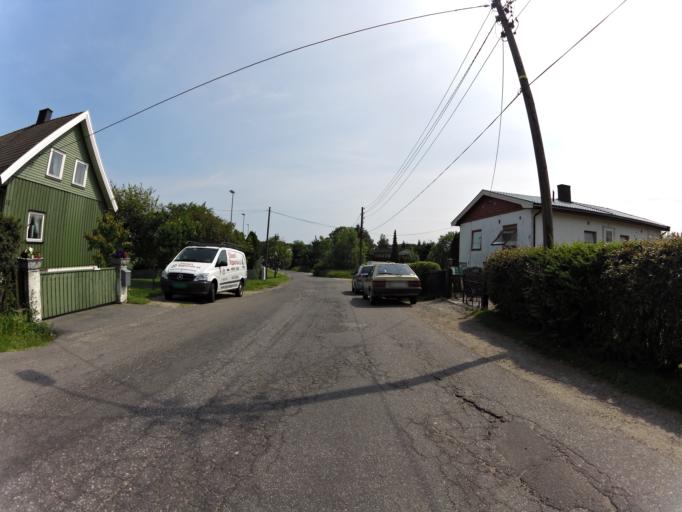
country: NO
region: Ostfold
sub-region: Fredrikstad
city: Fredrikstad
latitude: 59.2428
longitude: 10.9946
